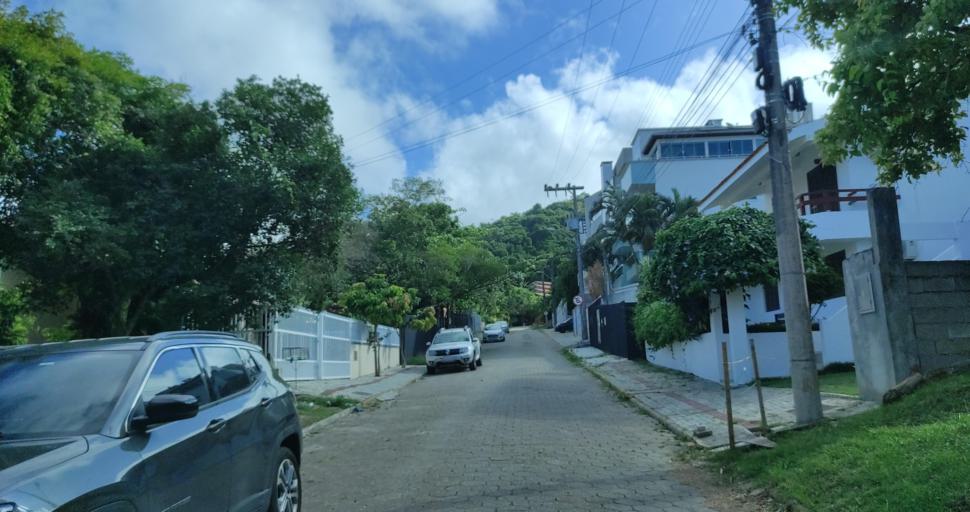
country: BR
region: Santa Catarina
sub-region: Porto Belo
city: Porto Belo
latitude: -27.1519
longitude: -48.4914
